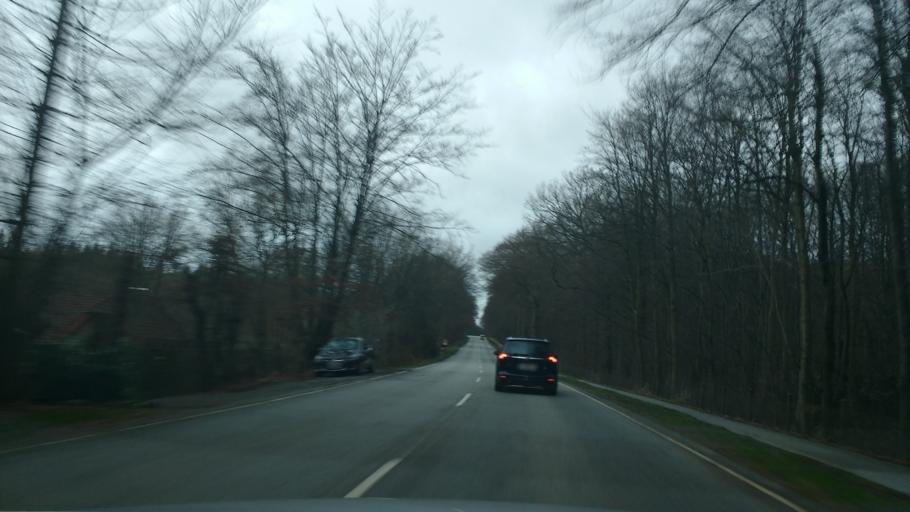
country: DE
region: Schleswig-Holstein
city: Itzehoe
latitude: 53.9348
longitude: 9.5387
